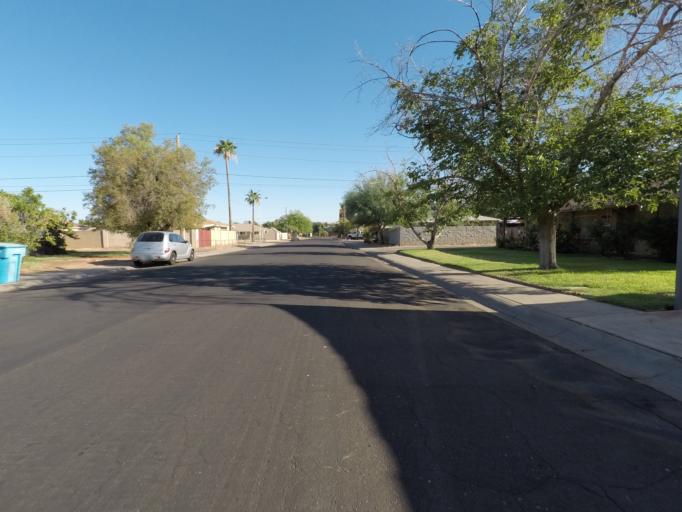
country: US
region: Arizona
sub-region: Maricopa County
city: Glendale
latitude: 33.5181
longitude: -112.1300
